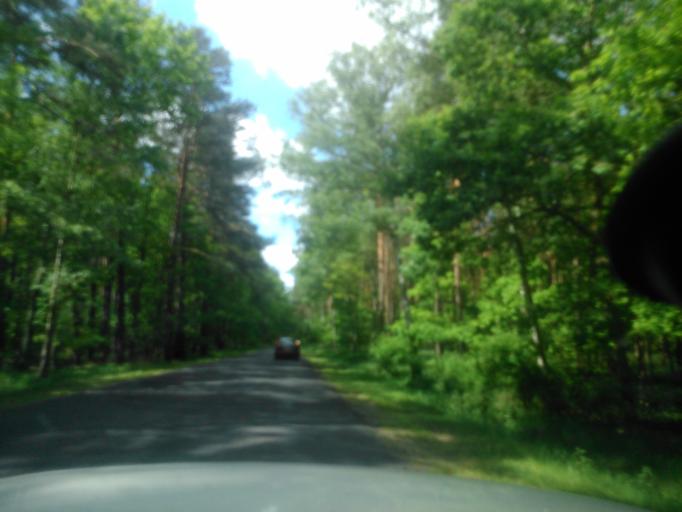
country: PL
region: Kujawsko-Pomorskie
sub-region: Powiat golubsko-dobrzynski
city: Ciechocin
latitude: 53.0768
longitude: 18.9696
